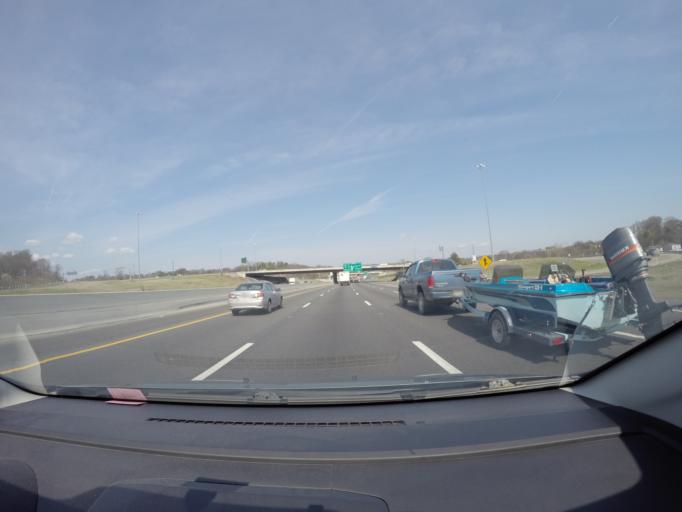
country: US
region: Tennessee
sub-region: Davidson County
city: Oak Hill
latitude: 36.1085
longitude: -86.7208
